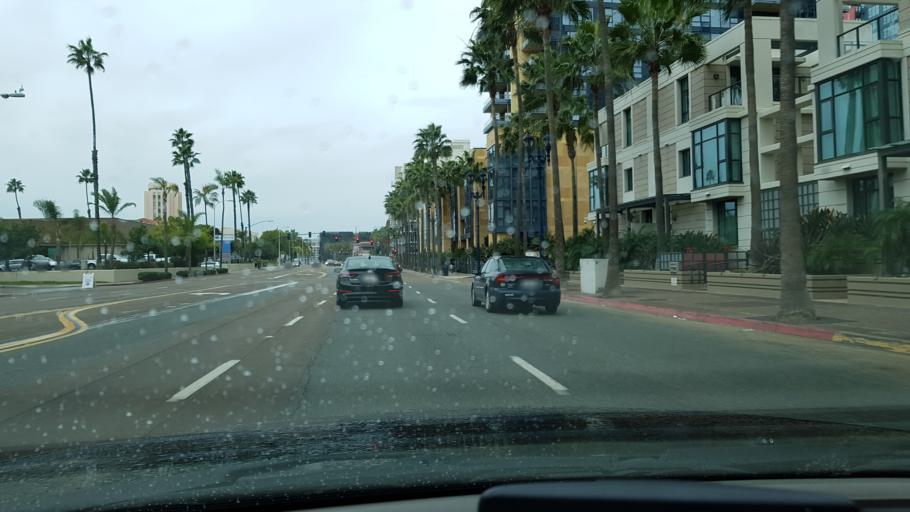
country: US
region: California
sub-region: San Diego County
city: San Diego
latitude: 32.7183
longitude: -117.1709
